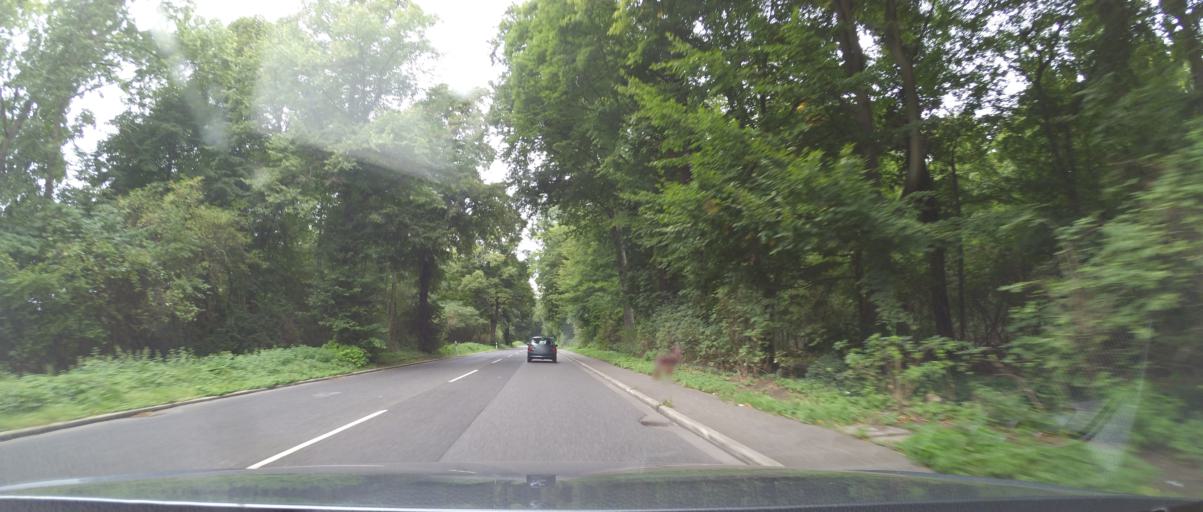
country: DE
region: North Rhine-Westphalia
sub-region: Regierungsbezirk Koln
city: Hurth
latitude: 50.9246
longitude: 6.8841
